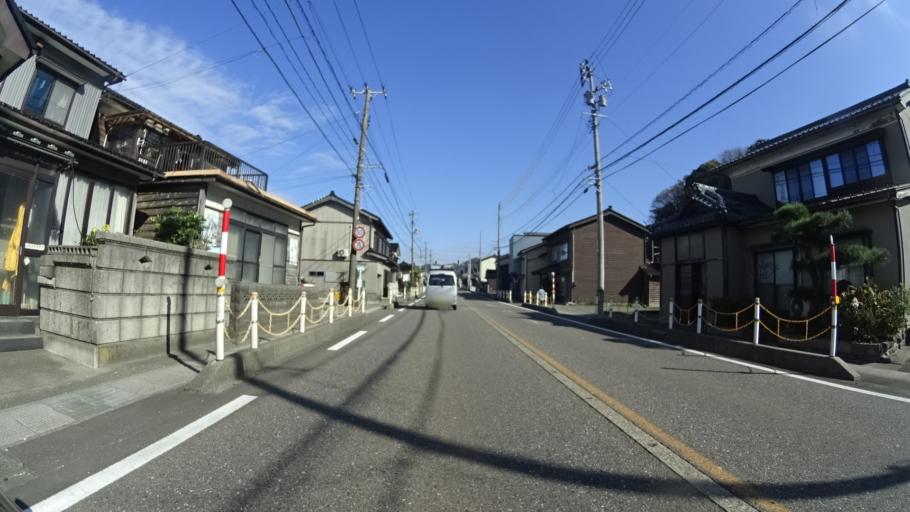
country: JP
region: Niigata
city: Itoigawa
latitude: 37.0657
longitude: 137.9226
